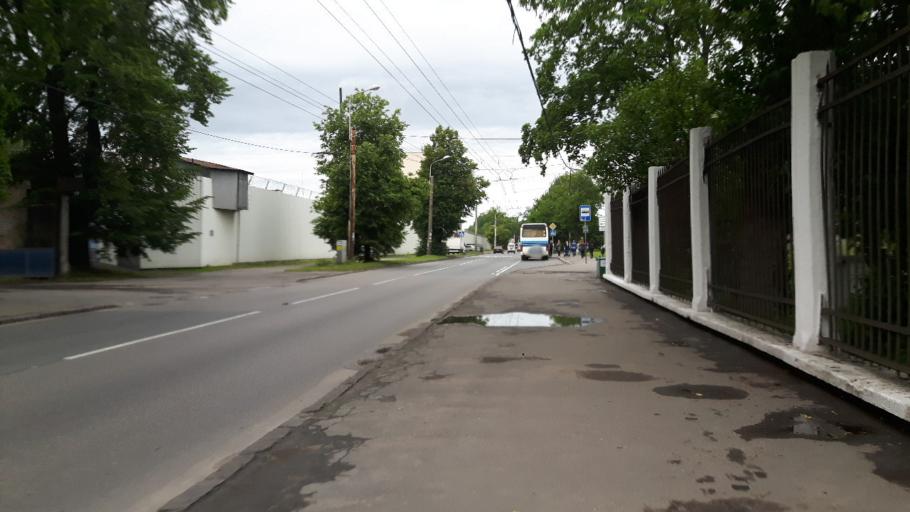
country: RU
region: Kaliningrad
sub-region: Gorod Kaliningrad
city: Kaliningrad
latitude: 54.7393
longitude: 20.4780
